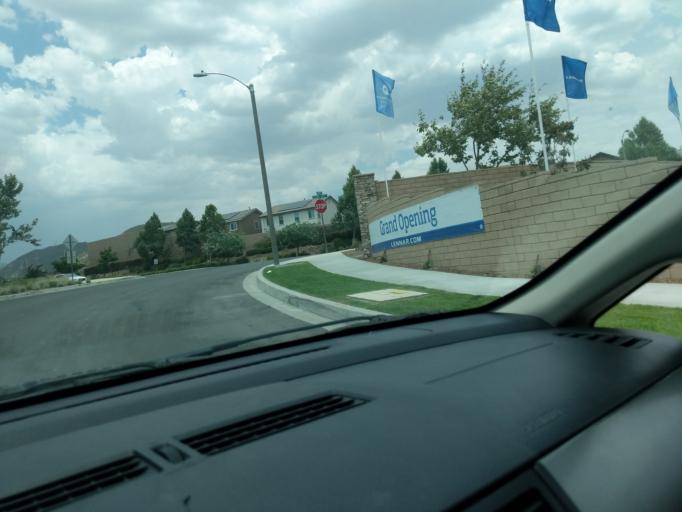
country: US
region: California
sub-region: San Bernardino County
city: Muscoy
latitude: 34.1862
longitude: -117.4277
